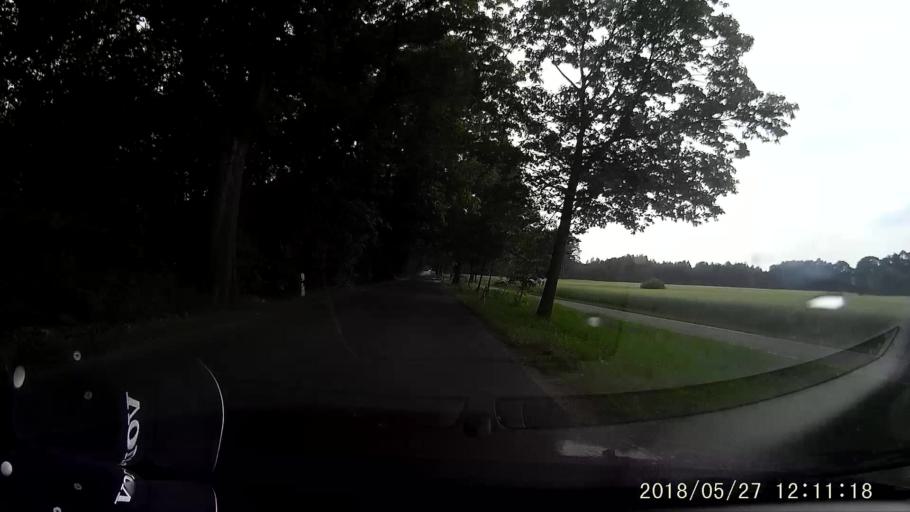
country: DE
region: Saxony
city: Klitten
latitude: 51.3576
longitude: 14.5756
